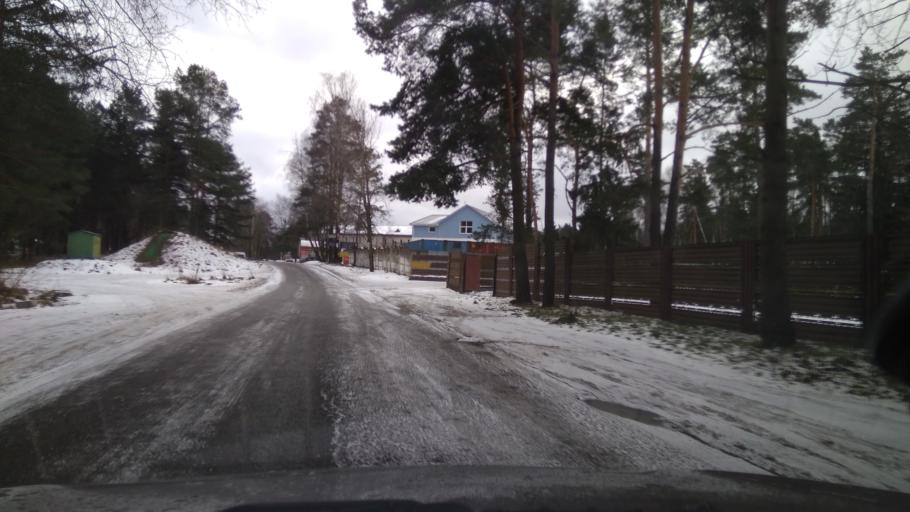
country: BY
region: Minsk
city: Borovlyany
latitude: 53.9627
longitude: 27.6477
